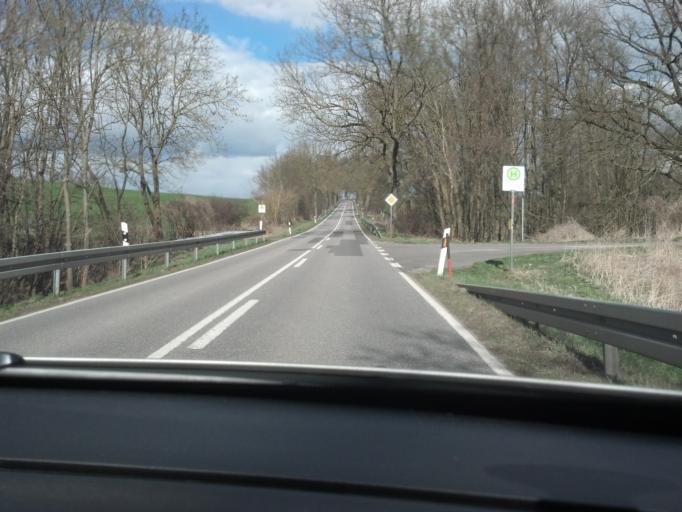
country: DE
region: Mecklenburg-Vorpommern
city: Loitz
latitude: 53.4029
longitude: 13.3624
